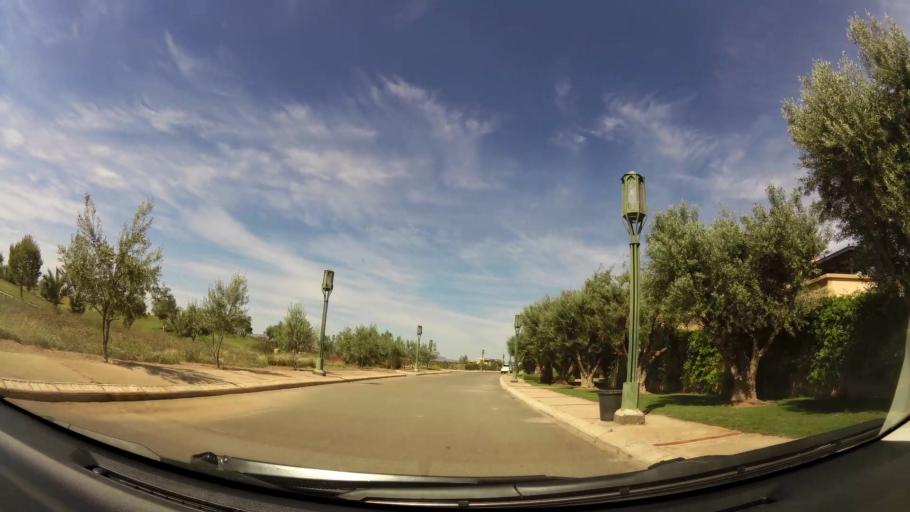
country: MA
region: Marrakech-Tensift-Al Haouz
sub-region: Marrakech
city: Marrakesh
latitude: 31.6155
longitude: -7.9288
